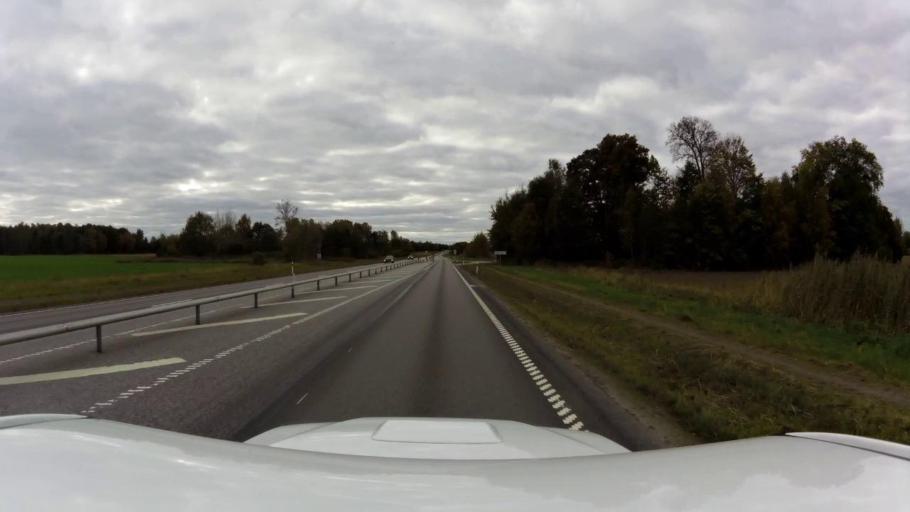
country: SE
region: OEstergoetland
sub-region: Linkopings Kommun
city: Malmslatt
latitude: 58.3722
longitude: 15.5435
